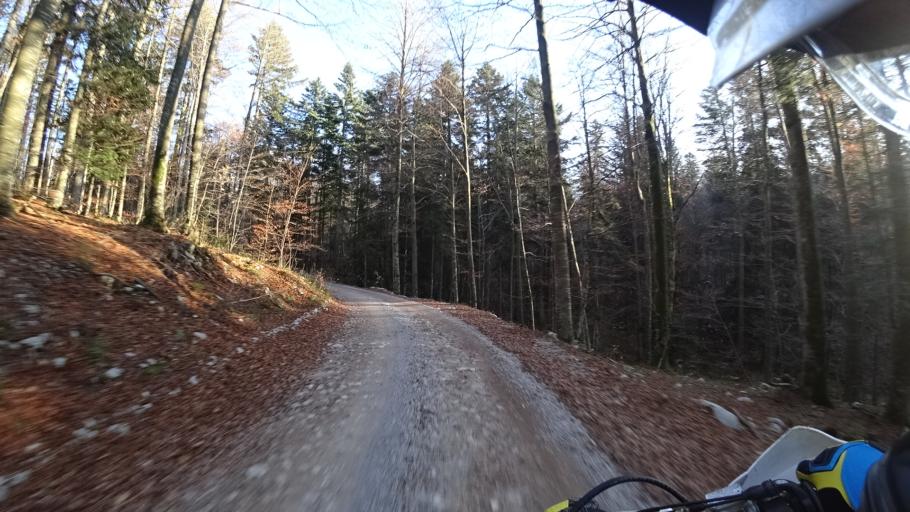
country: HR
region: Primorsko-Goranska
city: Drazice
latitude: 45.4839
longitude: 14.4666
